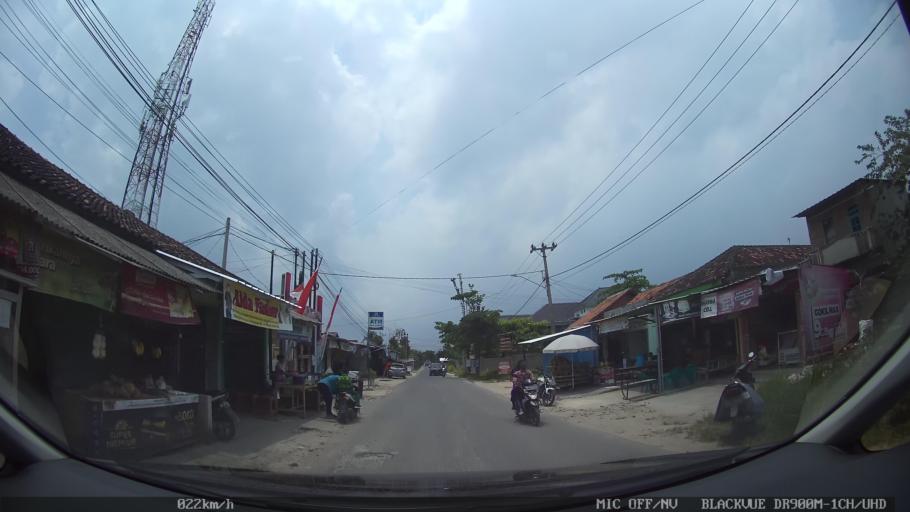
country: ID
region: Lampung
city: Kedaton
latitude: -5.3944
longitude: 105.3073
